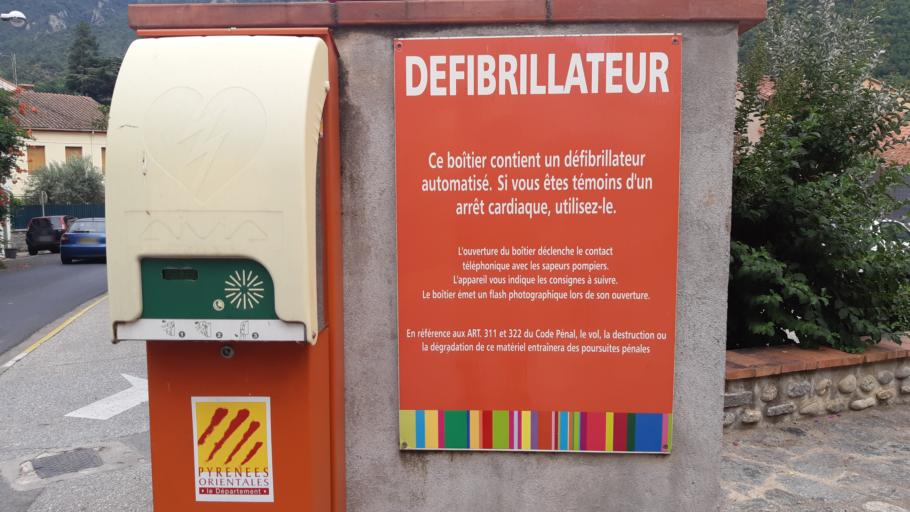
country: FR
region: Languedoc-Roussillon
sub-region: Departement des Pyrenees-Orientales
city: Arles
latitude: 42.4559
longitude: 2.6339
